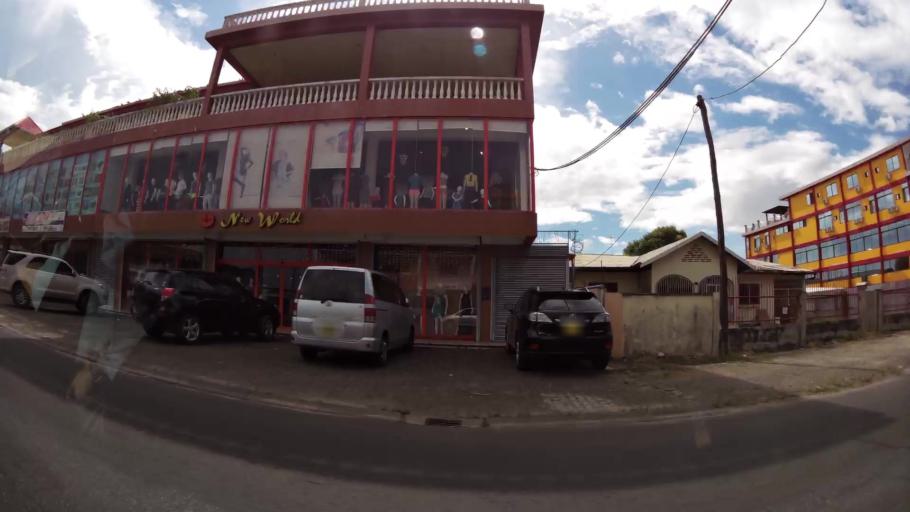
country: SR
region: Paramaribo
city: Paramaribo
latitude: 5.8459
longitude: -55.1417
